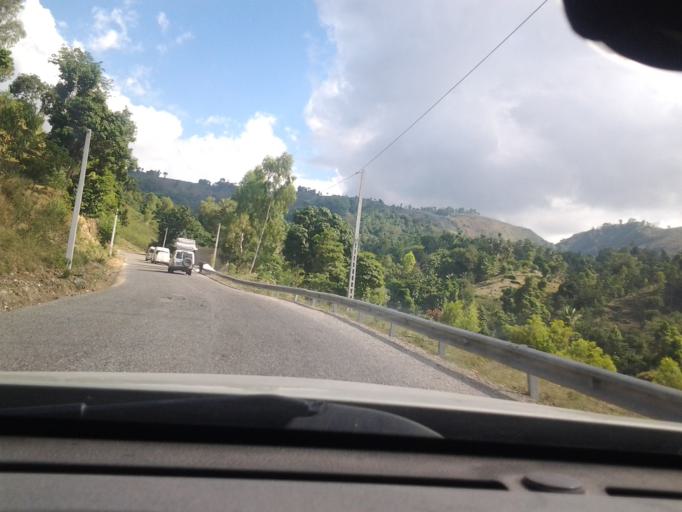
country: HT
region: Ouest
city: Leogane
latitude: 18.3848
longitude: -72.6059
